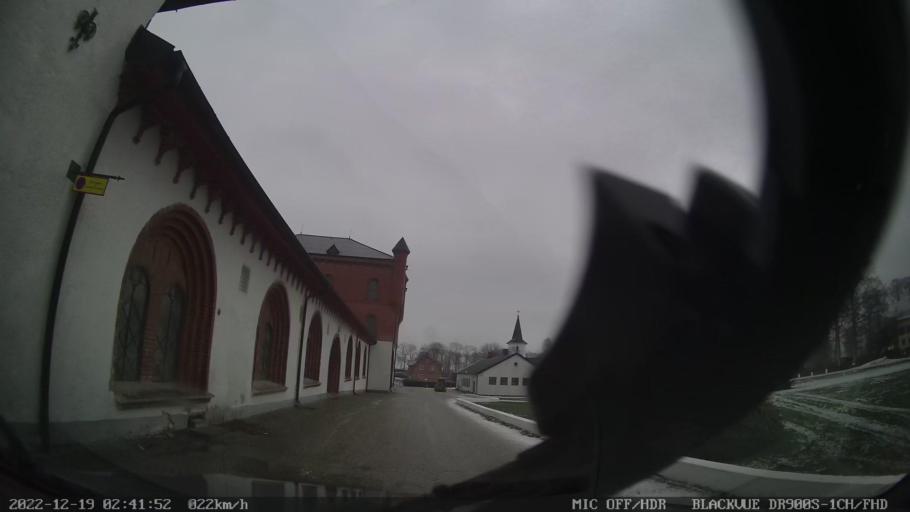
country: SE
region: Skane
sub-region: Tomelilla Kommun
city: Tomelilla
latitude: 55.4922
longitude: 14.0446
